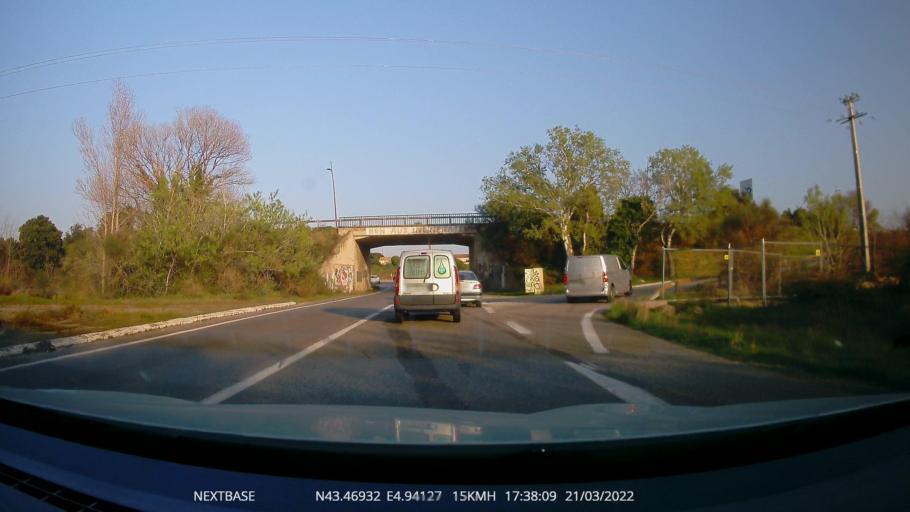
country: FR
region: Provence-Alpes-Cote d'Azur
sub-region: Departement des Bouches-du-Rhone
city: Fos-sur-Mer
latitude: 43.4693
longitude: 4.9413
